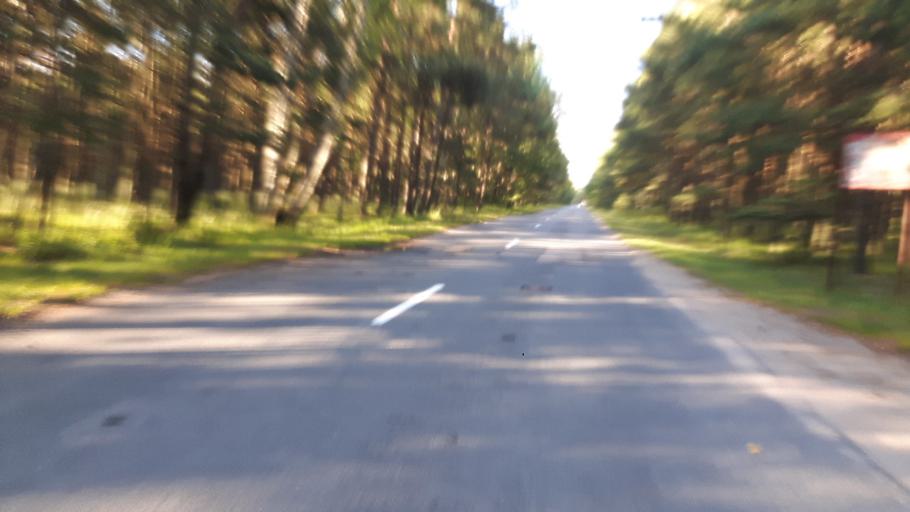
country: LT
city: Nida
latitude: 55.2332
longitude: 20.9051
